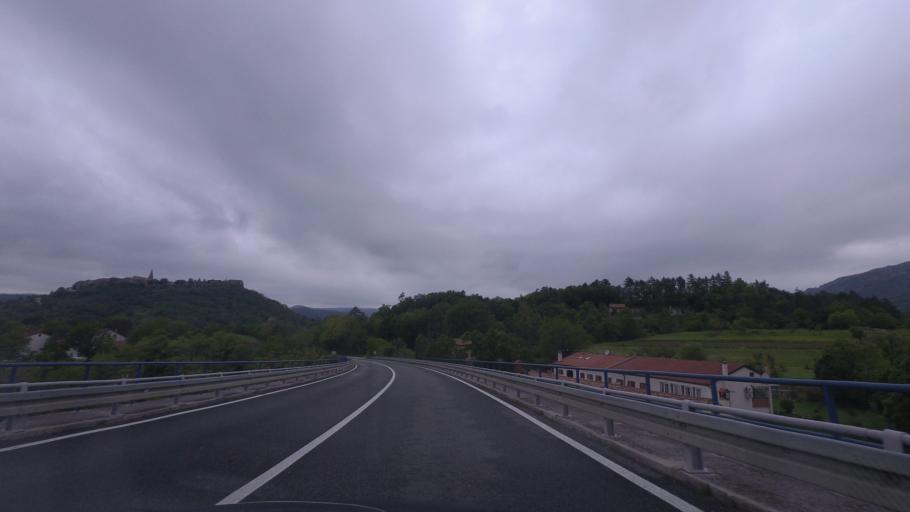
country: HR
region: Istarska
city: Buzet
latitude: 45.4060
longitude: 13.9803
